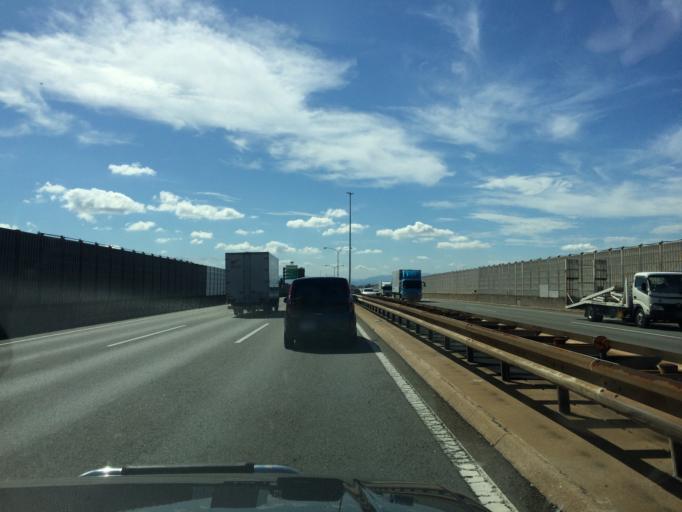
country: JP
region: Osaka
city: Yao
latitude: 34.6640
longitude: 135.5983
